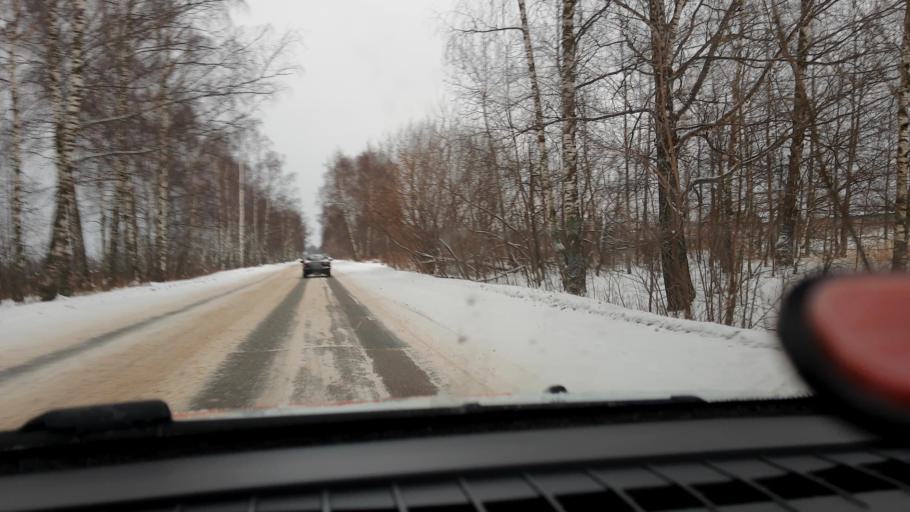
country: RU
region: Nizjnij Novgorod
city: Pamyat' Parizhskoy Kommuny
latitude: 56.2684
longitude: 44.4257
